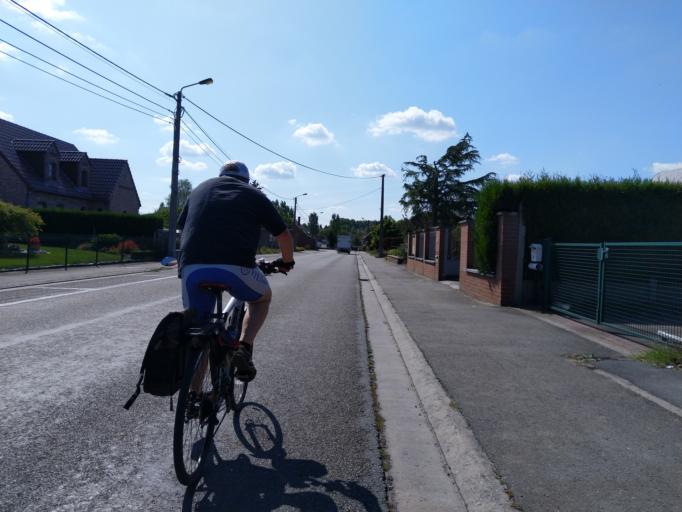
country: BE
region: Wallonia
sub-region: Province du Hainaut
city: Saint-Ghislain
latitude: 50.4647
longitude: 3.8408
